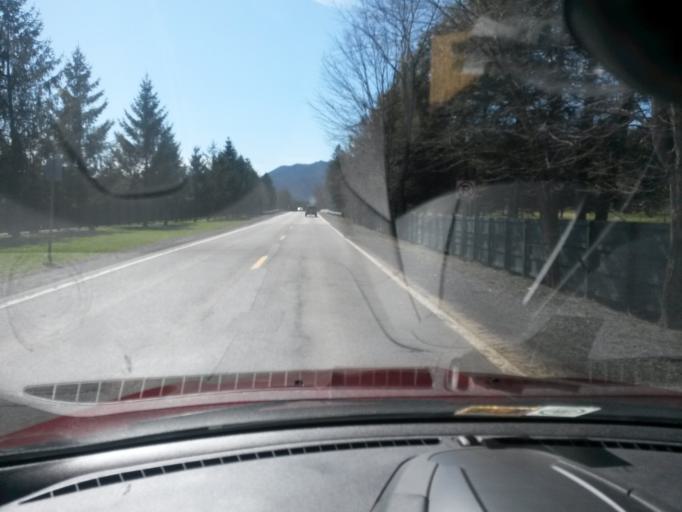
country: US
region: West Virginia
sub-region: Greenbrier County
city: White Sulphur Springs
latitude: 37.7792
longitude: -80.3241
